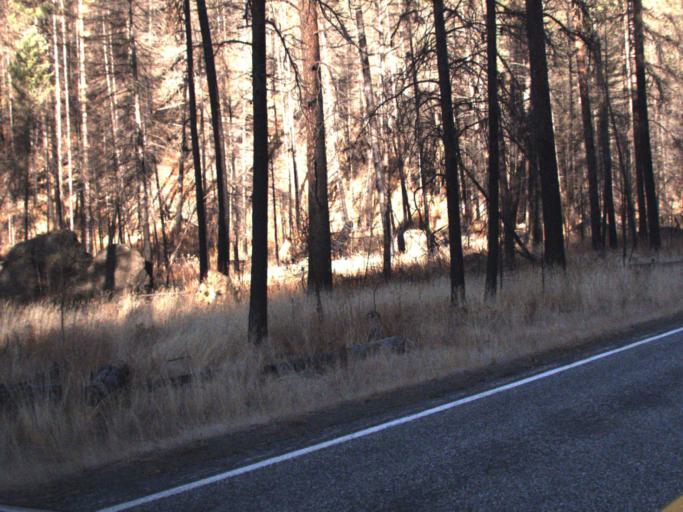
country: US
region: Washington
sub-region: Ferry County
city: Republic
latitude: 48.4046
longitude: -118.7331
